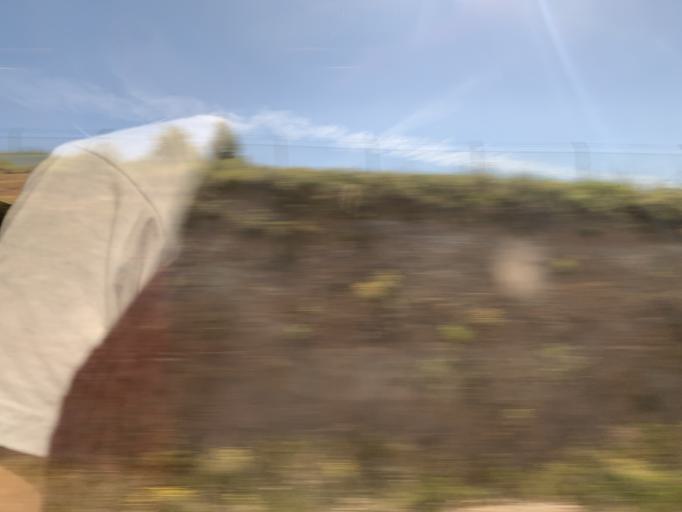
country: ES
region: Catalonia
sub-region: Provincia de Lleida
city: Arbeca
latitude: 41.4776
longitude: 0.8825
